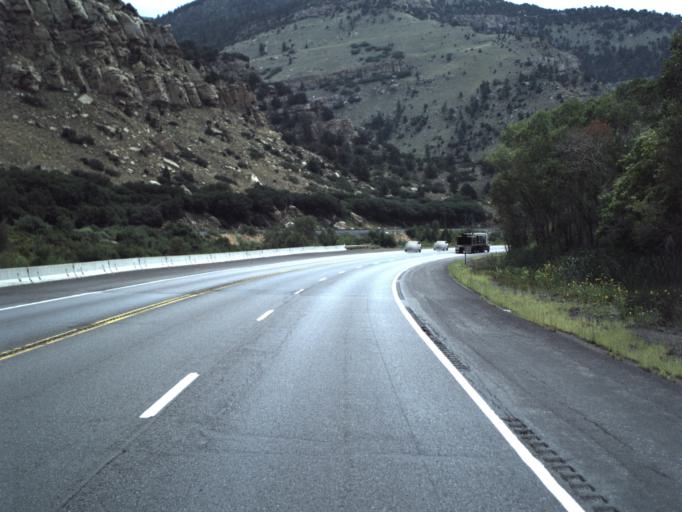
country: US
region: Utah
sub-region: Carbon County
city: Helper
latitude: 39.7636
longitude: -110.8988
